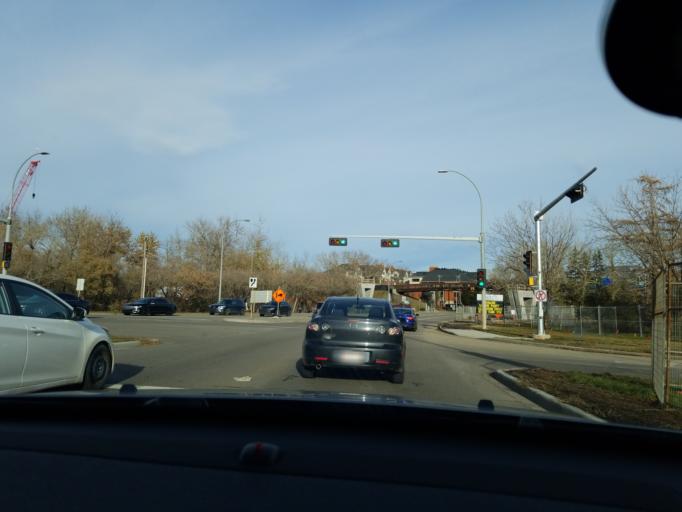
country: CA
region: Alberta
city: Edmonton
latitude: 53.5374
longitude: -113.4788
